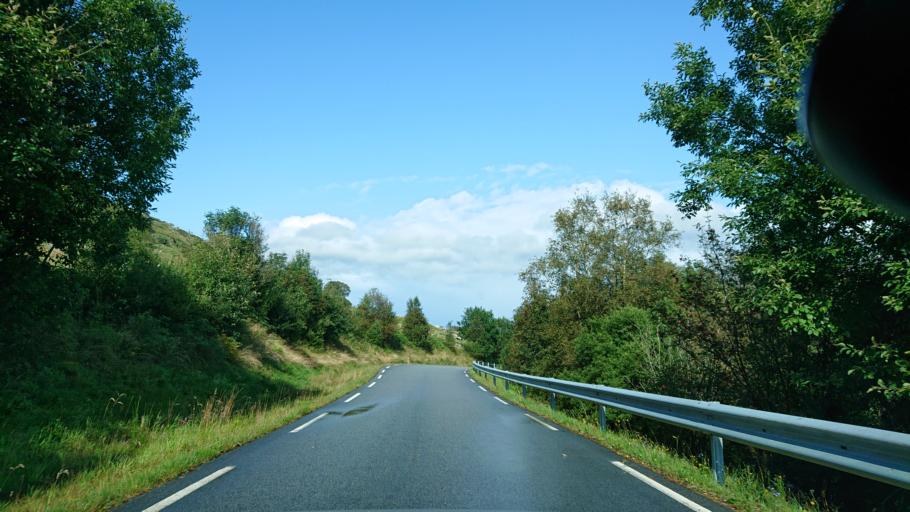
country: NO
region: Rogaland
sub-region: Gjesdal
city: Algard
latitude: 58.6898
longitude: 5.8767
